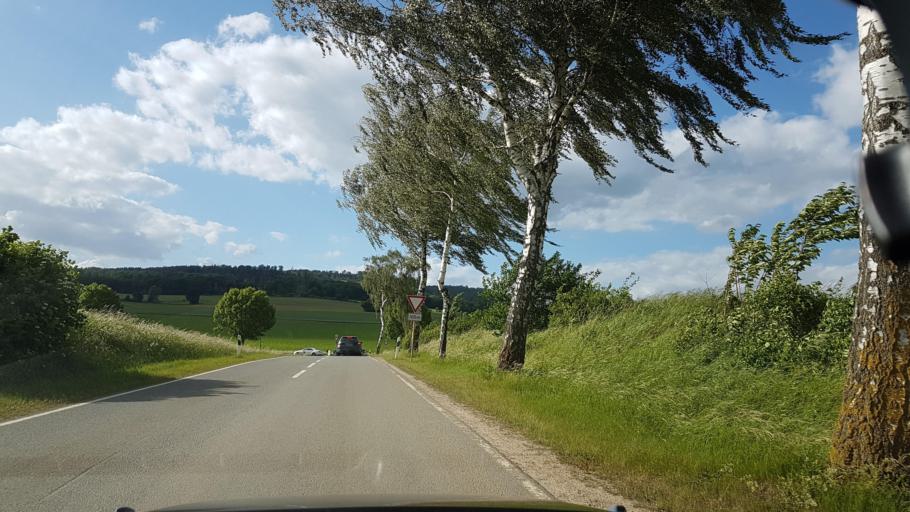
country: DE
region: Lower Saxony
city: Heinsen
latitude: 52.1020
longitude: 9.6712
